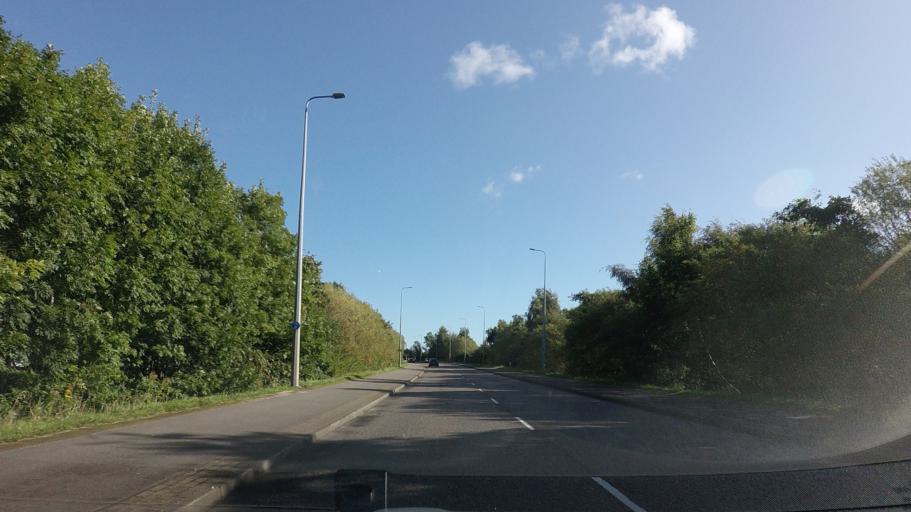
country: GB
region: Scotland
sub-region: Highland
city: Inverness
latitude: 57.4577
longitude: -4.2036
